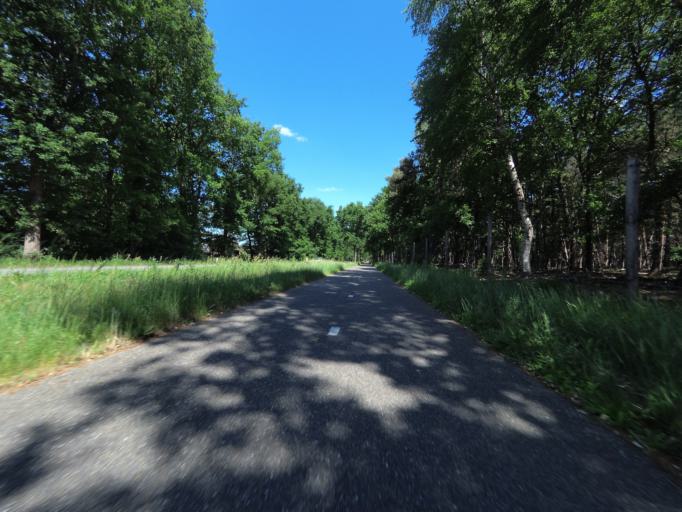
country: NL
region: Gelderland
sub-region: Gemeente Ede
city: Otterlo
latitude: 52.1158
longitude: 5.7657
